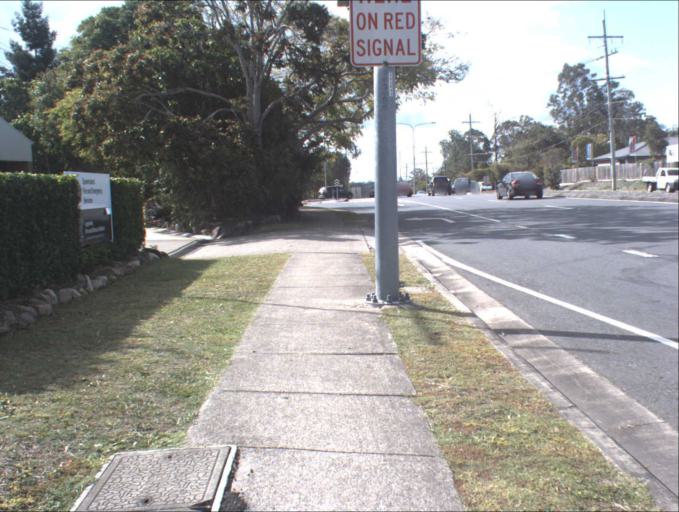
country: AU
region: Queensland
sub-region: Logan
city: Waterford West
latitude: -27.6827
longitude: 153.1217
